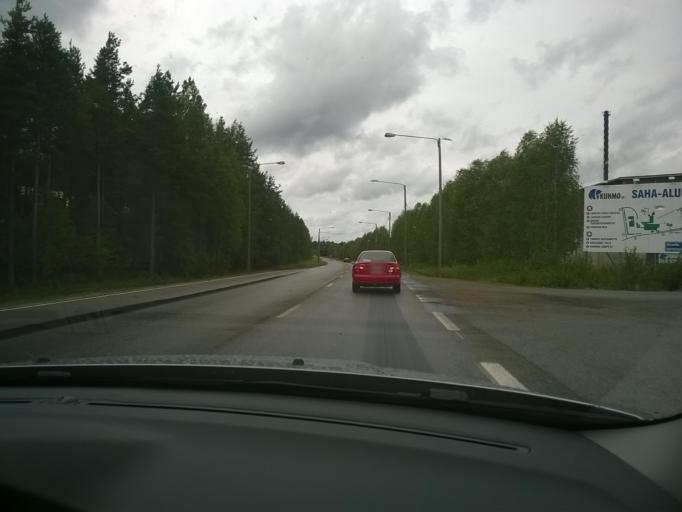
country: FI
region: Kainuu
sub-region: Kehys-Kainuu
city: Kuhmo
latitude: 64.1306
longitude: 29.4946
